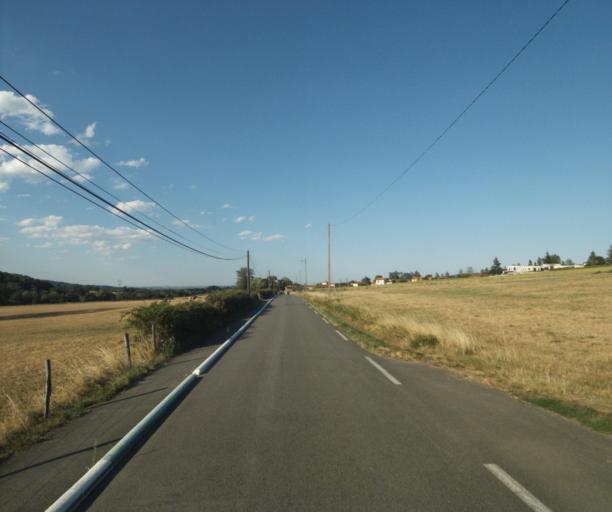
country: FR
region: Rhone-Alpes
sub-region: Departement du Rhone
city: Lentilly
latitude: 45.8271
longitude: 4.6729
